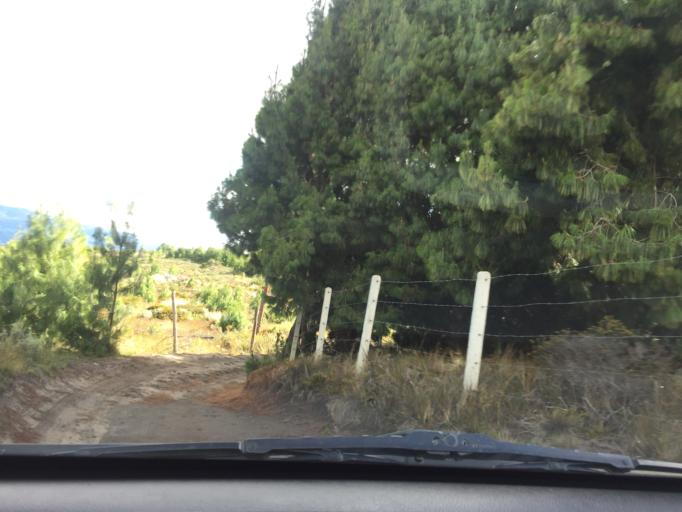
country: CO
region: Cundinamarca
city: Tocancipa
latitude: 4.9410
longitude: -73.8982
